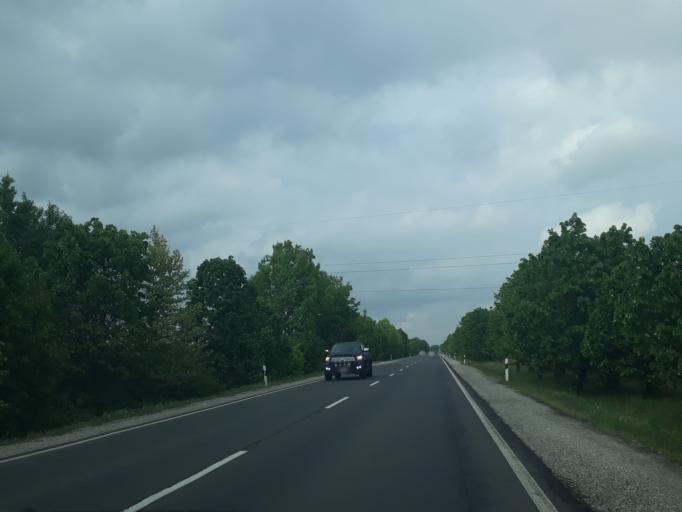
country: HU
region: Szabolcs-Szatmar-Bereg
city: Ajak
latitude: 48.1978
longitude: 22.0456
